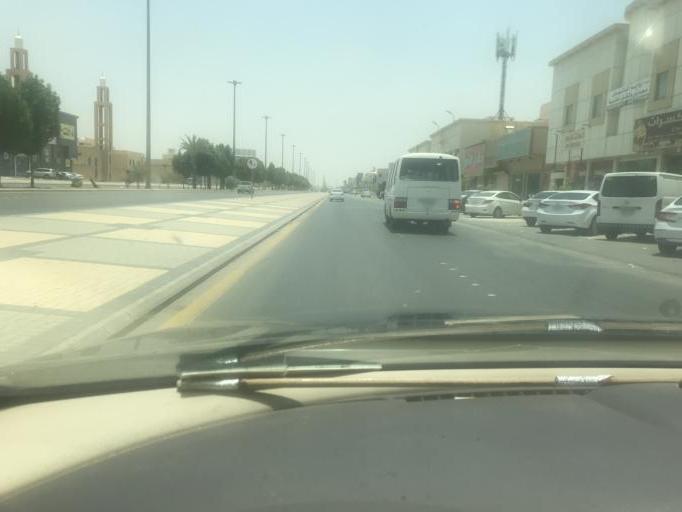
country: SA
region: Ar Riyad
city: Riyadh
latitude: 24.8208
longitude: 46.7512
